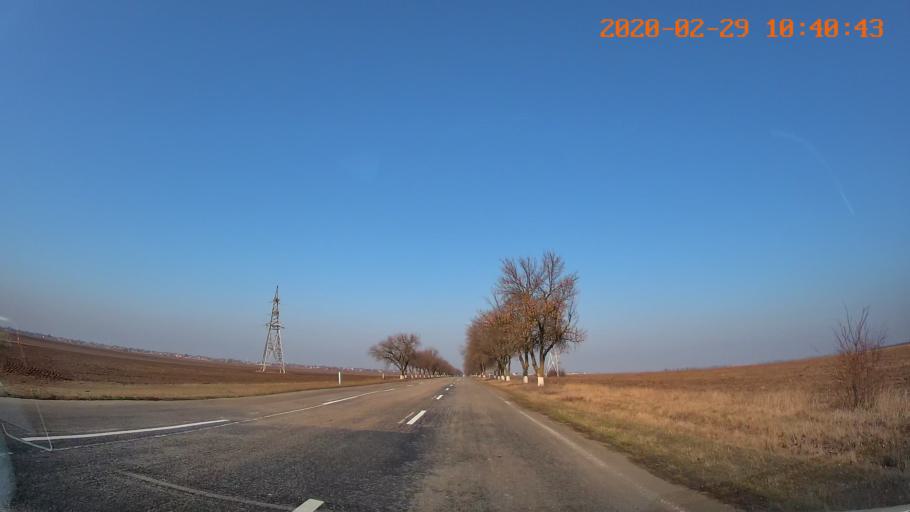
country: MD
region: Anenii Noi
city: Varnita
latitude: 47.0356
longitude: 29.4356
